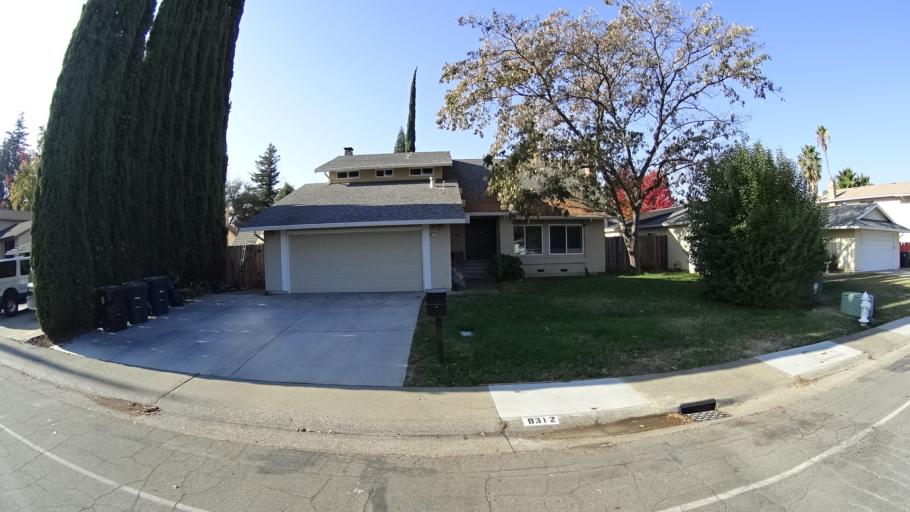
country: US
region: California
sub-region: Sacramento County
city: Citrus Heights
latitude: 38.7127
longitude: -121.2552
